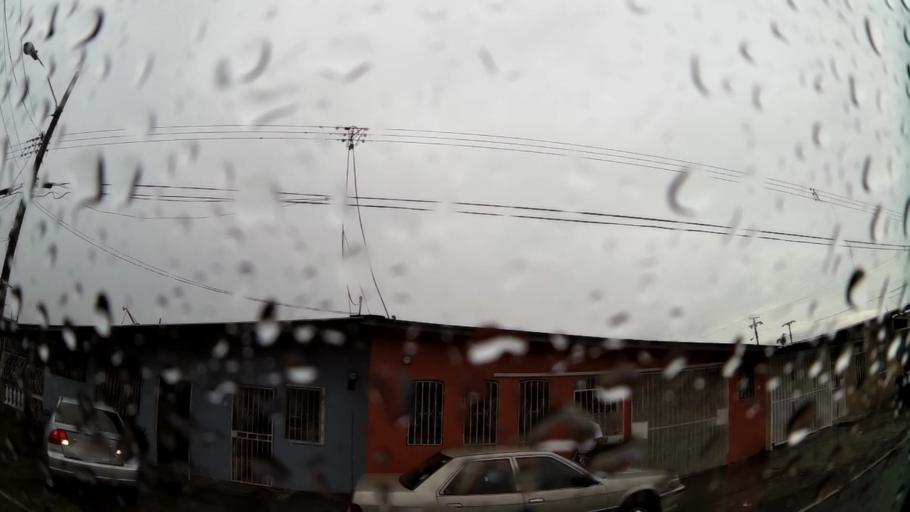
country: PA
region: Colon
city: Sabanitas
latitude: 9.3539
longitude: -79.8084
